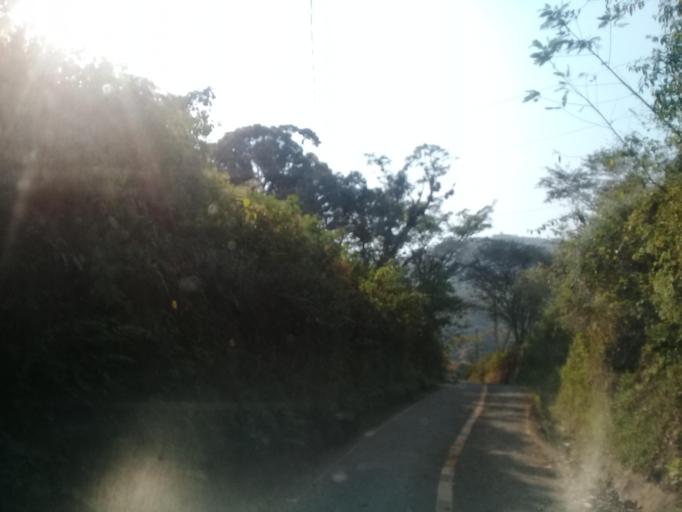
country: MX
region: Veracruz
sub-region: Ixtaczoquitlan
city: Campo Chico
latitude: 18.8352
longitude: -97.0344
